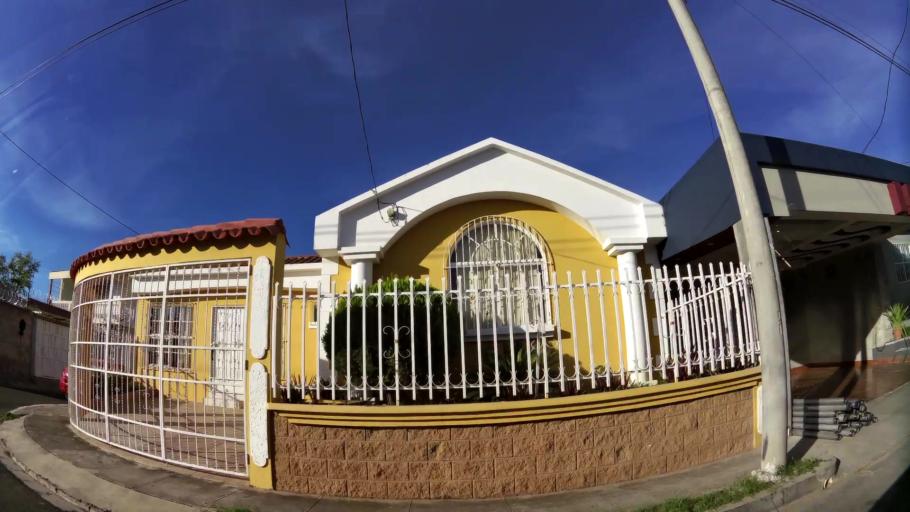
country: SV
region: San Miguel
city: San Miguel
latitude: 13.4593
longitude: -88.1698
